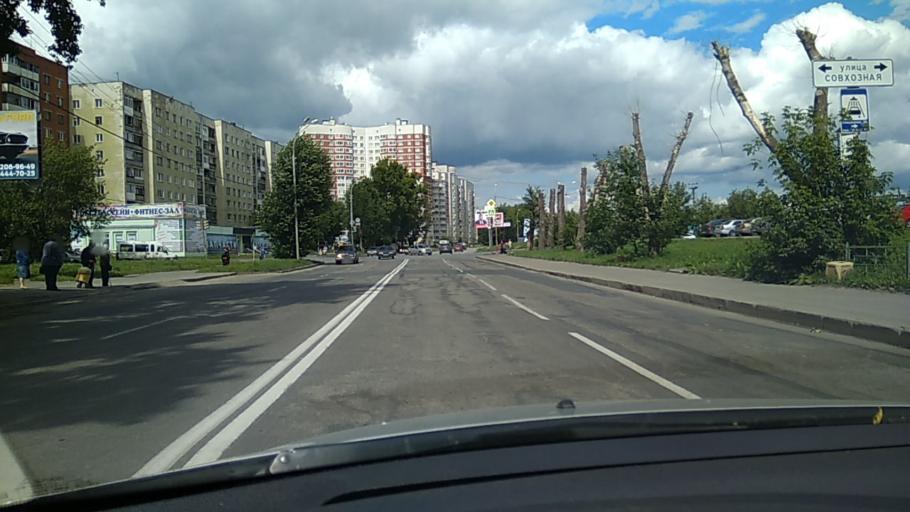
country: RU
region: Sverdlovsk
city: Yekaterinburg
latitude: 56.9070
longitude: 60.6208
